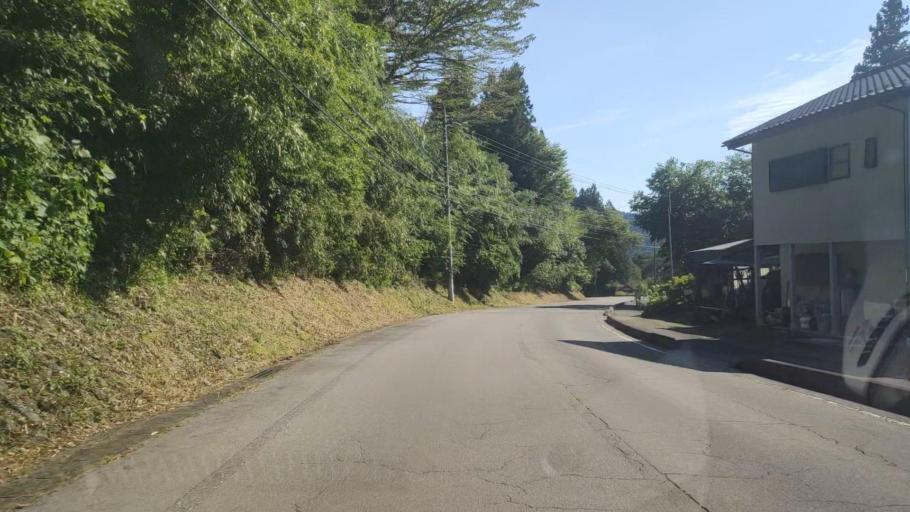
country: JP
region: Gunma
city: Nakanojomachi
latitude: 36.6087
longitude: 138.7267
